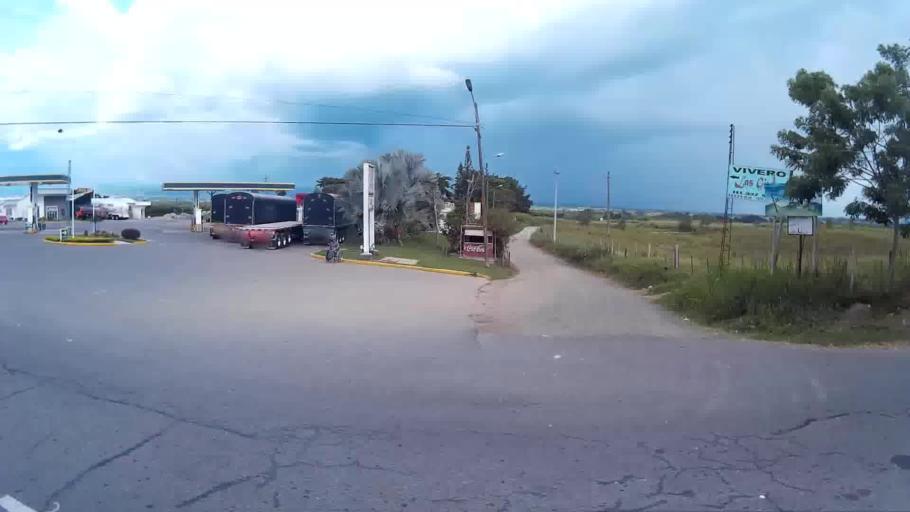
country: CO
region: Risaralda
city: La Virginia
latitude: 4.8090
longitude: -75.8120
